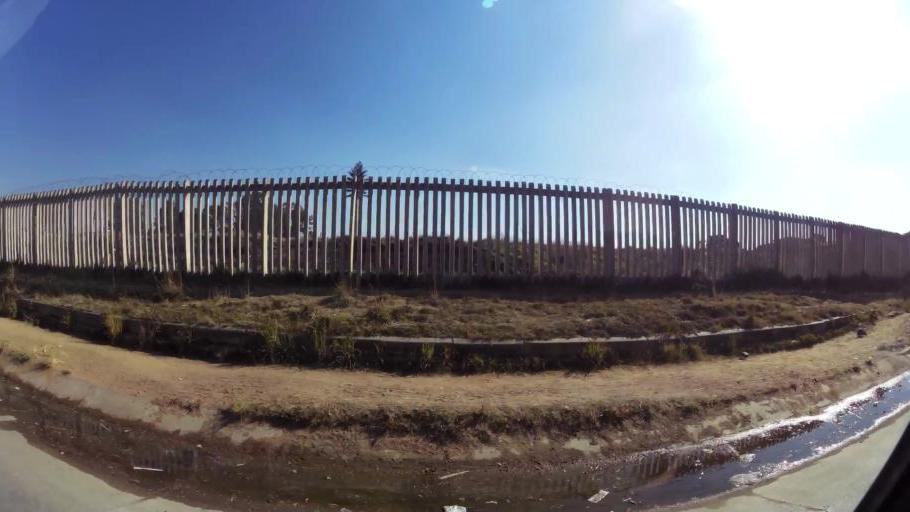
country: ZA
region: Gauteng
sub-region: West Rand District Municipality
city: Muldersdriseloop
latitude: -26.0200
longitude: 27.9292
